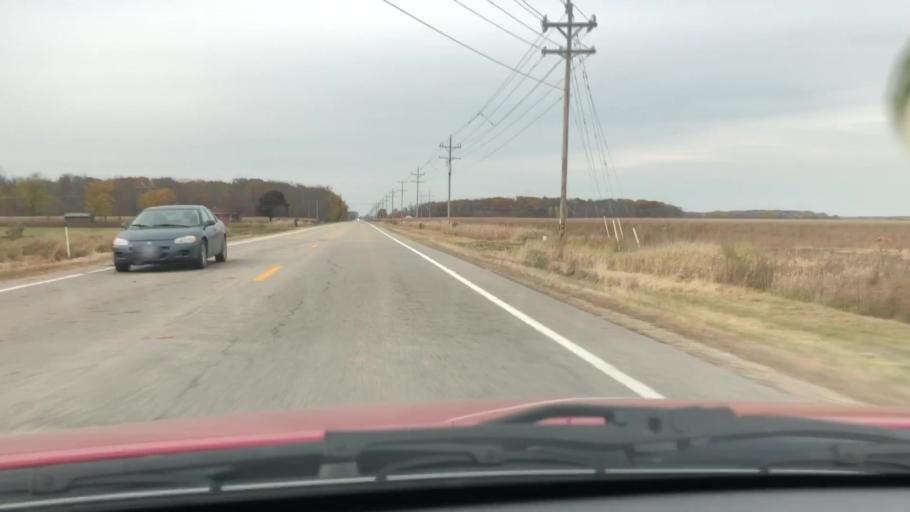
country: US
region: Wisconsin
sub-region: Outagamie County
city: Seymour
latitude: 44.4549
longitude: -88.2912
